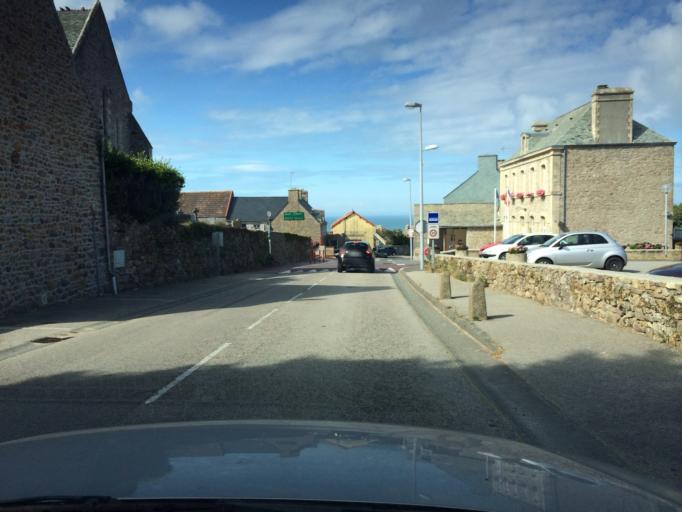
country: FR
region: Lower Normandy
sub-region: Departement de la Manche
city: Beaumont-Hague
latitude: 49.7109
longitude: -1.9321
